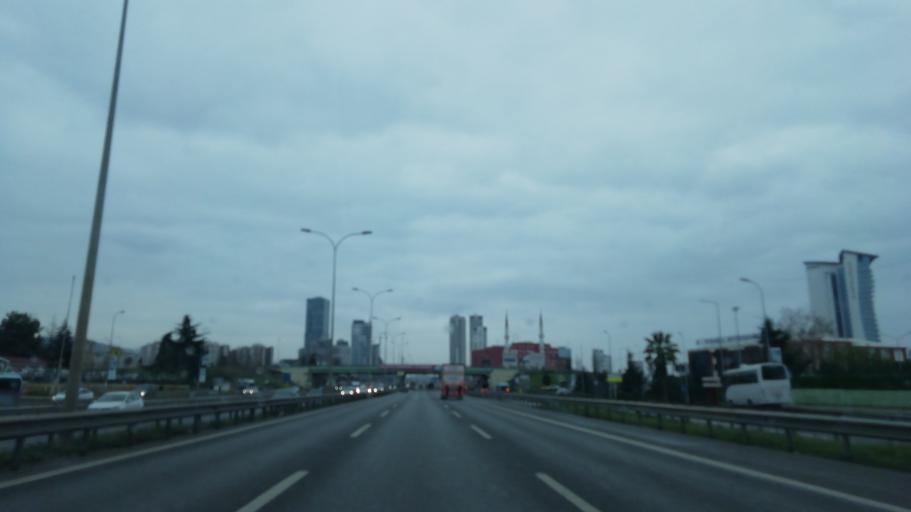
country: TR
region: Istanbul
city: Maltepe
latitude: 40.9142
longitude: 29.1868
